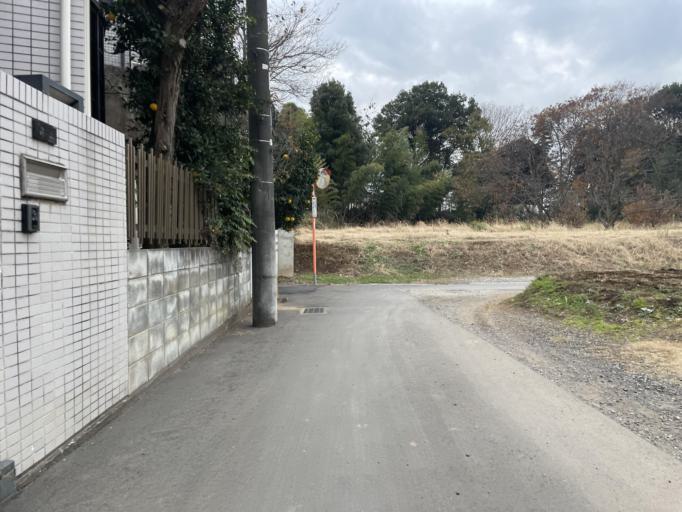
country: JP
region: Saitama
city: Shiraoka
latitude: 36.0010
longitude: 139.6602
